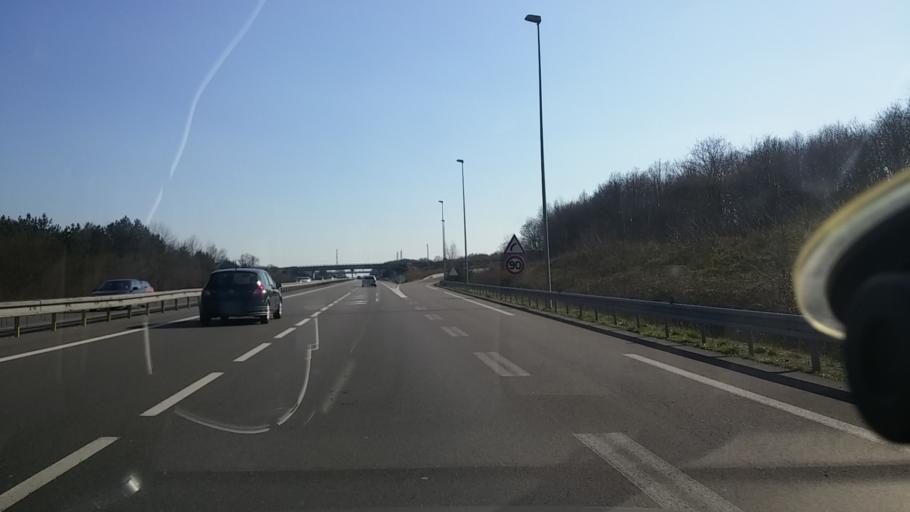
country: FR
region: Centre
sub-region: Departement du Loir-et-Cher
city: Theillay
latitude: 47.2931
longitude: 2.0441
